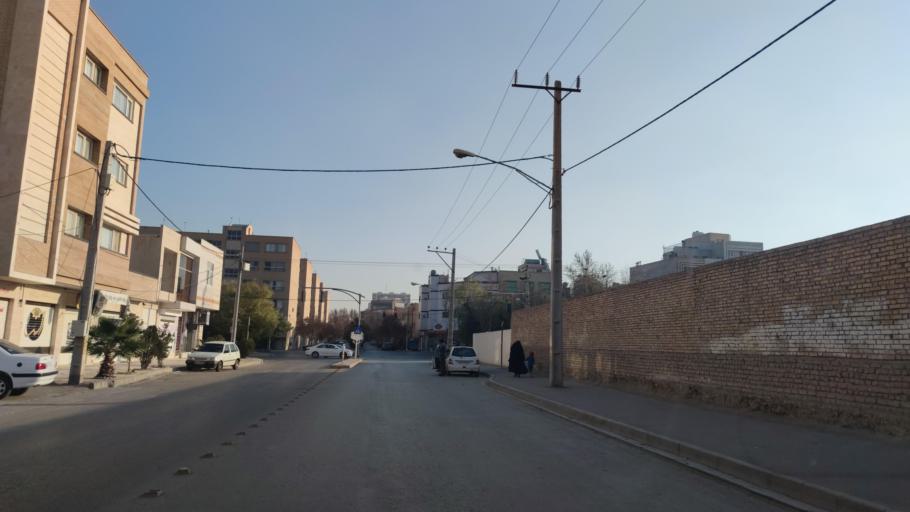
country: IR
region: Isfahan
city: Isfahan
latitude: 32.7101
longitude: 51.6856
